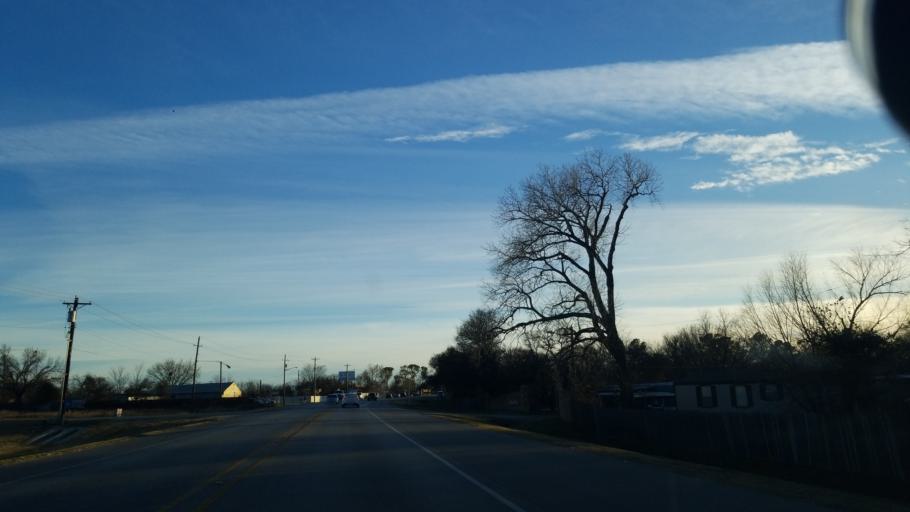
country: US
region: Texas
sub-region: Denton County
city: Denton
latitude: 33.1844
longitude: -97.1389
